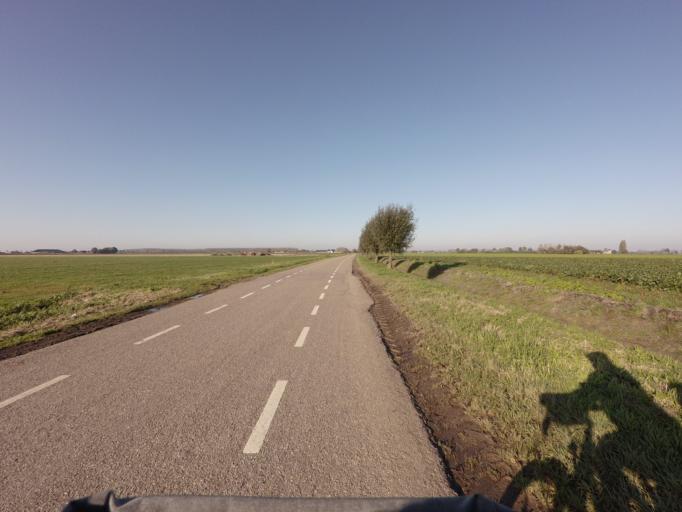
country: NL
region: North Brabant
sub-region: Gemeente Waalwijk
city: Waalwijk
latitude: 51.7457
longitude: 5.0607
